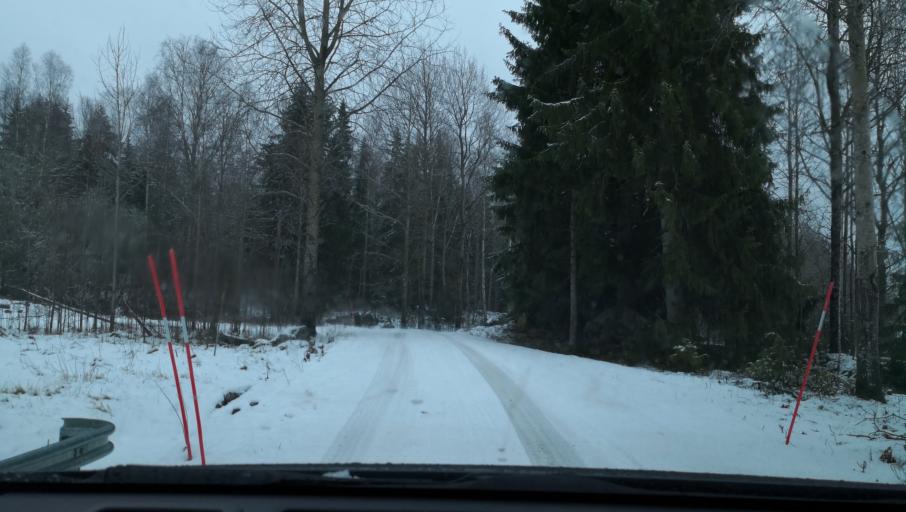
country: SE
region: Vaestmanland
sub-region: Kopings Kommun
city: Kolsva
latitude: 59.5650
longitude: 15.7838
